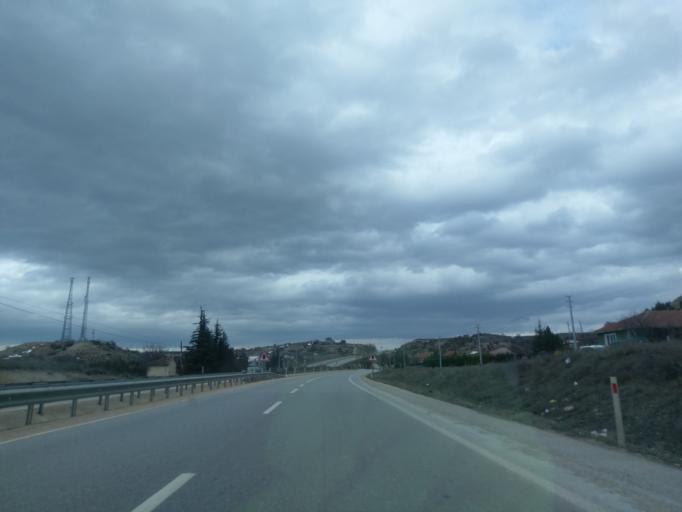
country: TR
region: Eskisehir
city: Eskisehir
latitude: 39.7325
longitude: 30.3813
